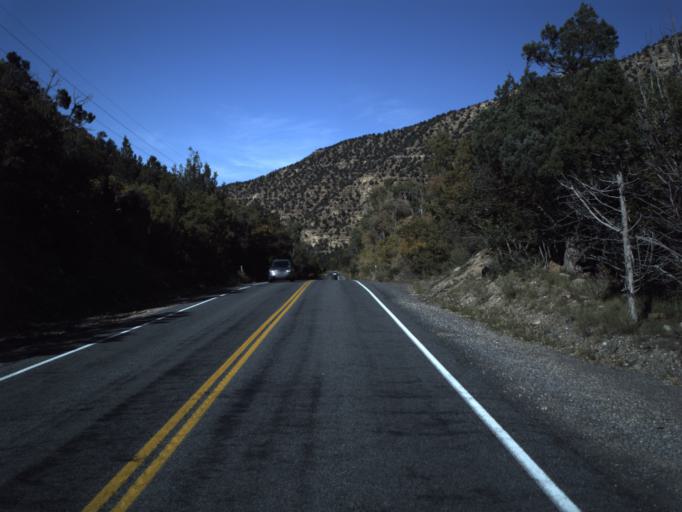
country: US
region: Utah
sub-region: Iron County
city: Parowan
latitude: 37.8027
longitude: -112.8129
